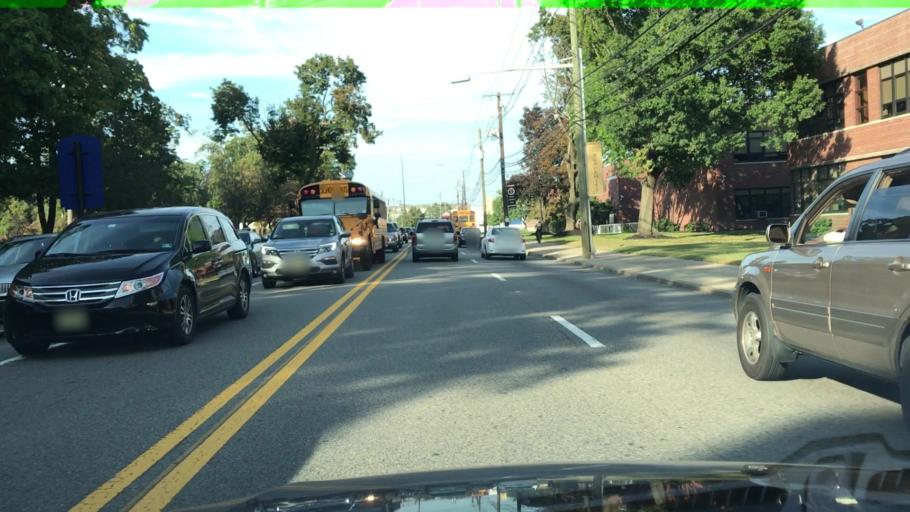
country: US
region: New Jersey
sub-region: Bergen County
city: Hackensack
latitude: 40.9024
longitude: -74.0347
